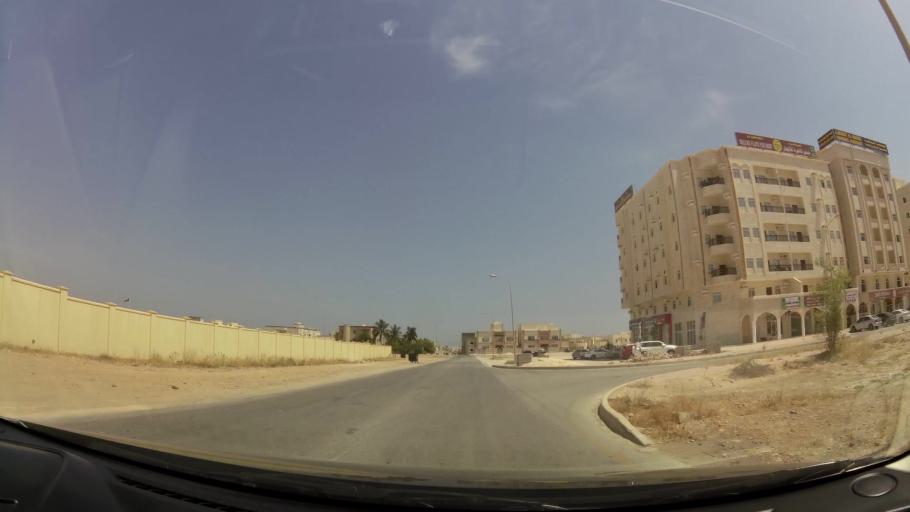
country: OM
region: Zufar
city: Salalah
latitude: 17.0515
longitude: 54.1571
